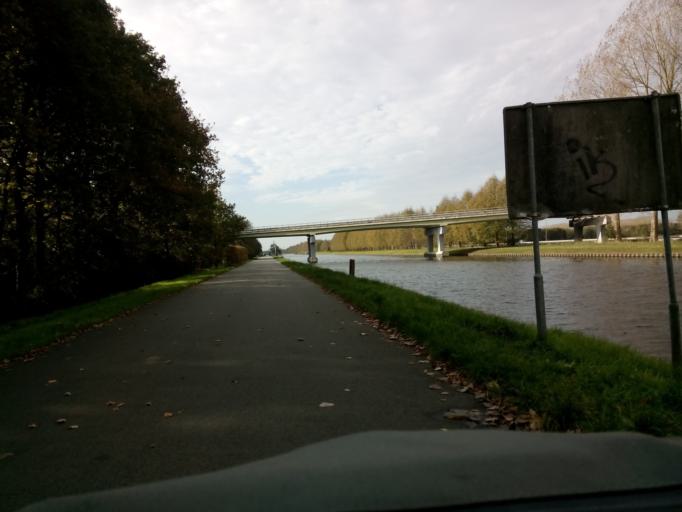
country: NL
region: Drenthe
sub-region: Gemeente Assen
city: Assen
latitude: 53.0193
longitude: 6.5508
